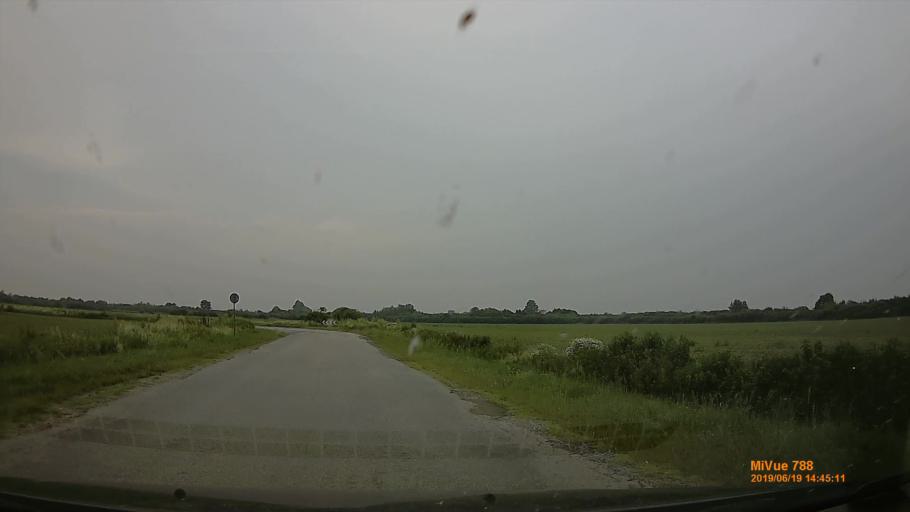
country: HU
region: Baranya
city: Szigetvar
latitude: 46.0228
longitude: 17.8228
